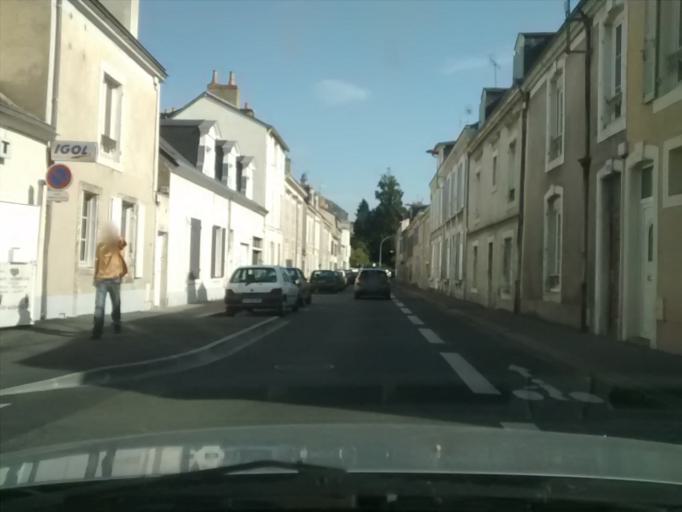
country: FR
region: Pays de la Loire
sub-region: Departement de la Sarthe
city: Le Mans
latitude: 48.0108
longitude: 0.1906
